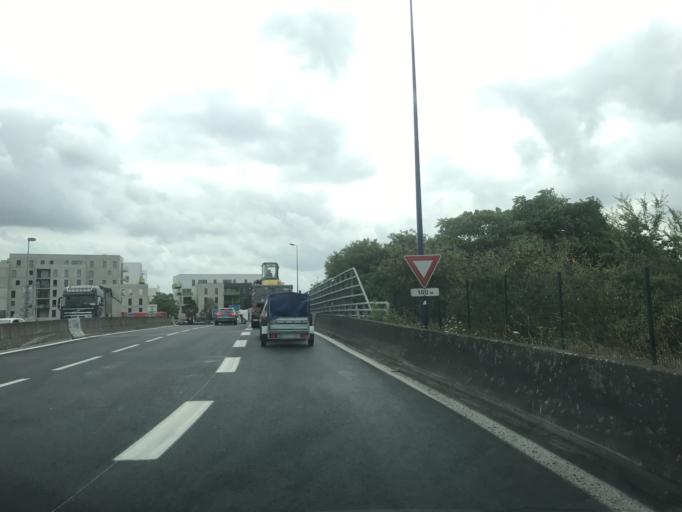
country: FR
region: Haute-Normandie
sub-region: Departement de la Seine-Maritime
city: Le Petit-Quevilly
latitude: 49.4360
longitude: 1.0715
